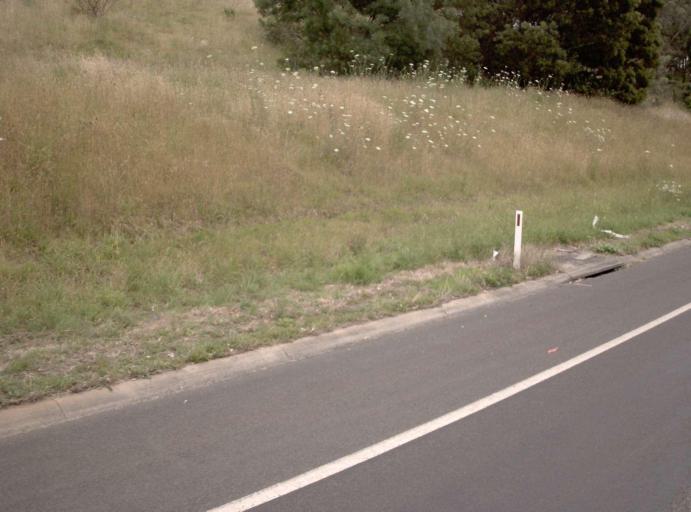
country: AU
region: Victoria
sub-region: Baw Baw
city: Warragul
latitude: -38.1361
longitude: 145.8818
